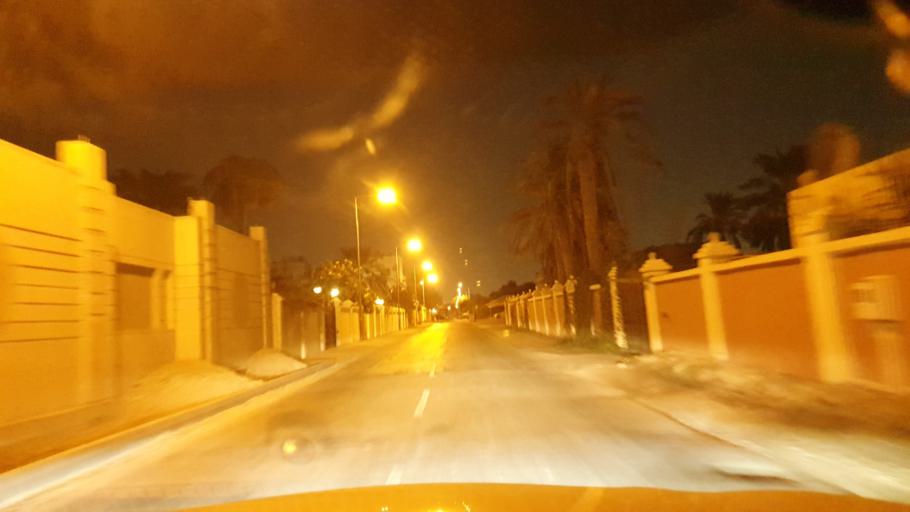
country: BH
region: Manama
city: Jidd Hafs
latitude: 26.1972
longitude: 50.4955
